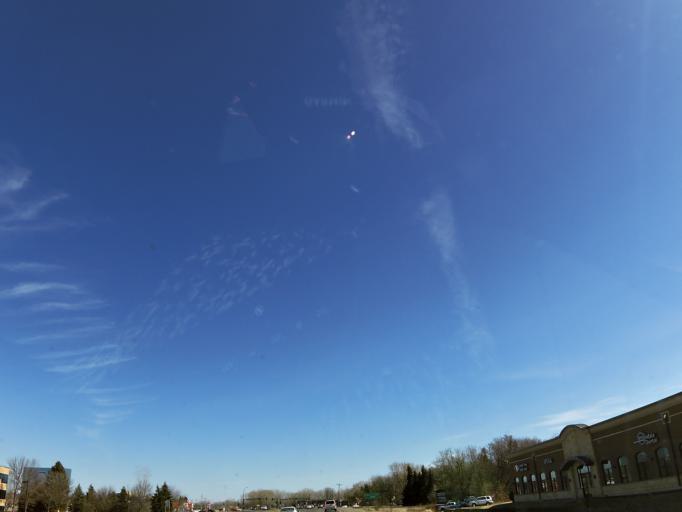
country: US
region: Minnesota
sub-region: Hennepin County
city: Plymouth
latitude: 44.9858
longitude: -93.4148
